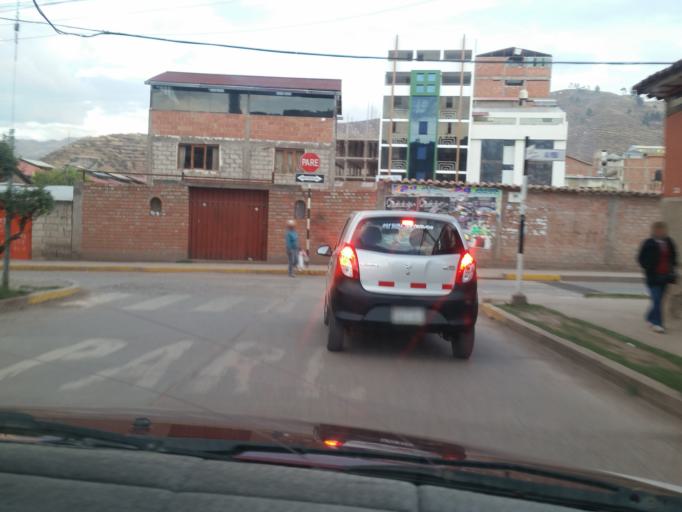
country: PE
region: Cusco
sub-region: Provincia de Cusco
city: Cusco
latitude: -13.5304
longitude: -71.9607
